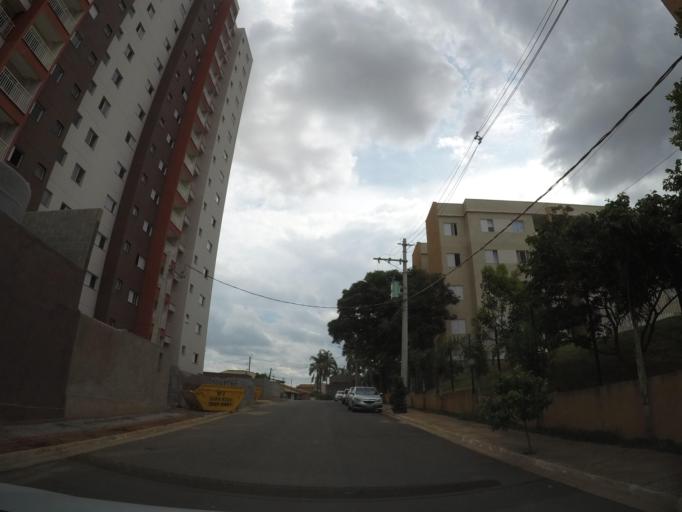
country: BR
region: Sao Paulo
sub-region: Sumare
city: Sumare
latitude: -22.8092
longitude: -47.2427
